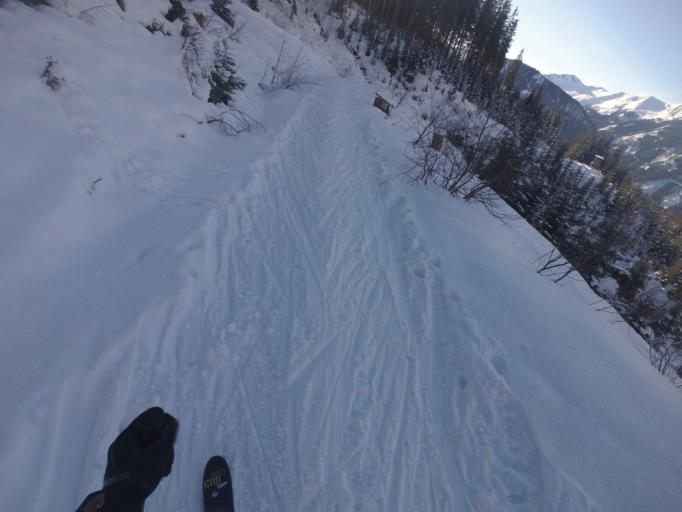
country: AT
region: Salzburg
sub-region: Politischer Bezirk Sankt Johann im Pongau
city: Huttschlag
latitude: 47.1799
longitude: 13.2747
